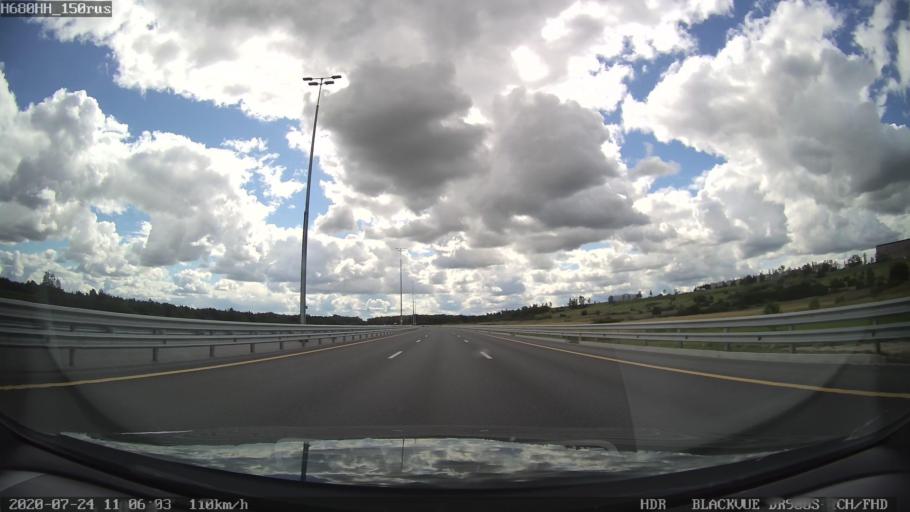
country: RU
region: St.-Petersburg
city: Shushary
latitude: 59.7688
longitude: 30.3662
